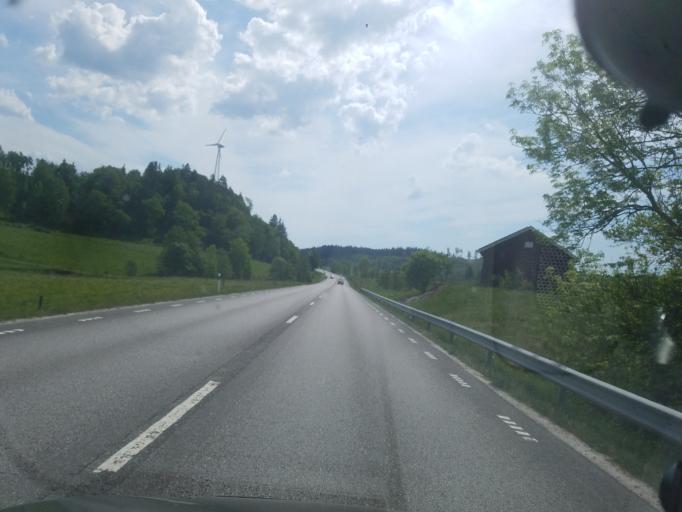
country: SE
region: Vaestra Goetaland
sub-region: Orust
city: Henan
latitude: 58.2057
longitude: 11.6907
